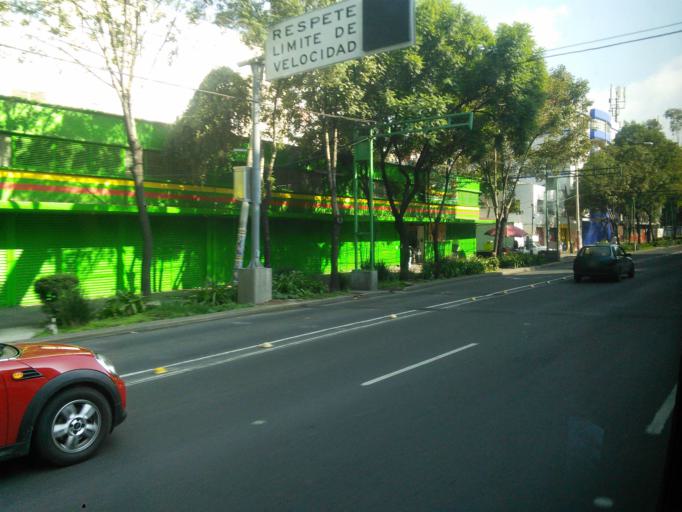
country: MX
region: Mexico City
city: Cuauhtemoc
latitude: 19.4483
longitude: -99.1387
